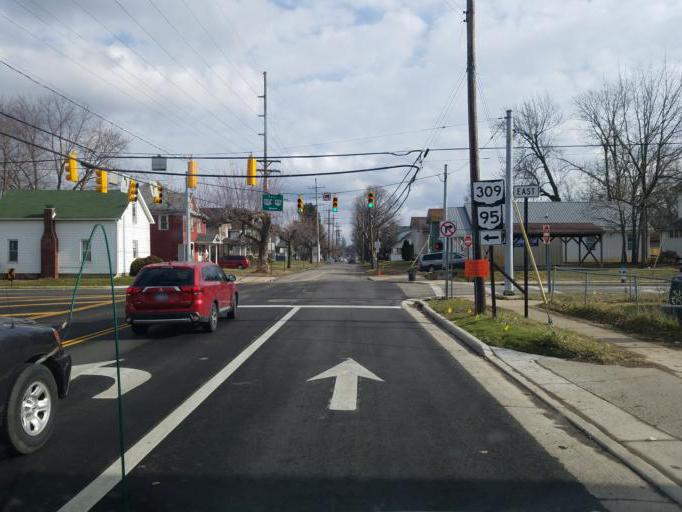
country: US
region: Ohio
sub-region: Marion County
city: Marion
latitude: 40.5845
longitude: -83.1369
